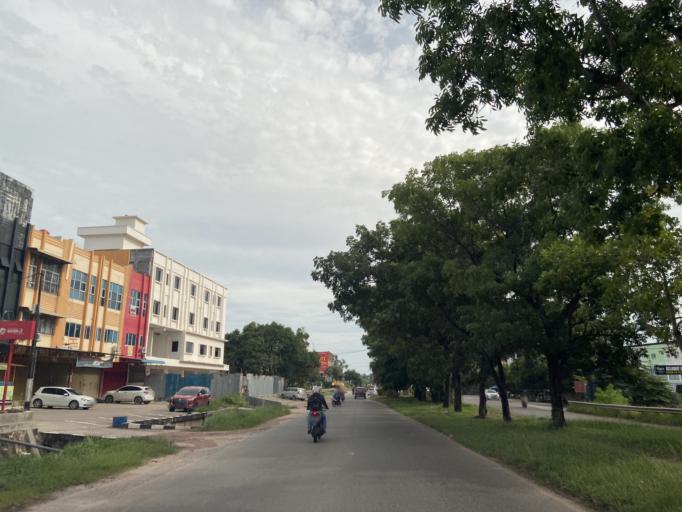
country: SG
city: Singapore
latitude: 1.1369
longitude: 104.0018
